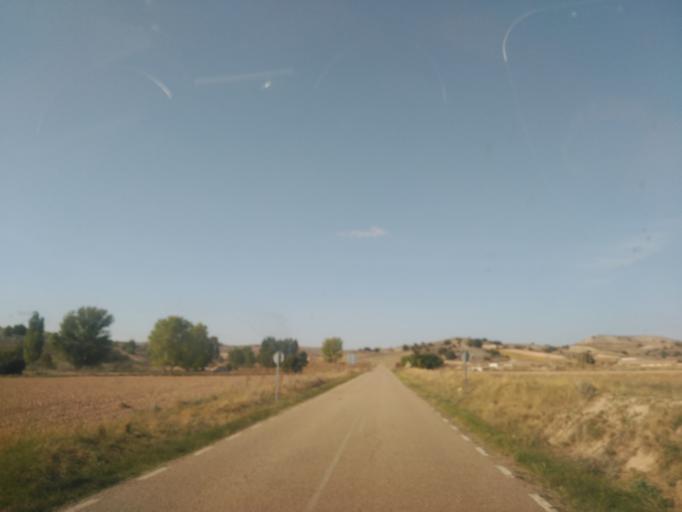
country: ES
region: Castille and Leon
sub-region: Provincia de Burgos
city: Penaranda de Duero
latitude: 41.6348
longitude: -3.4860
